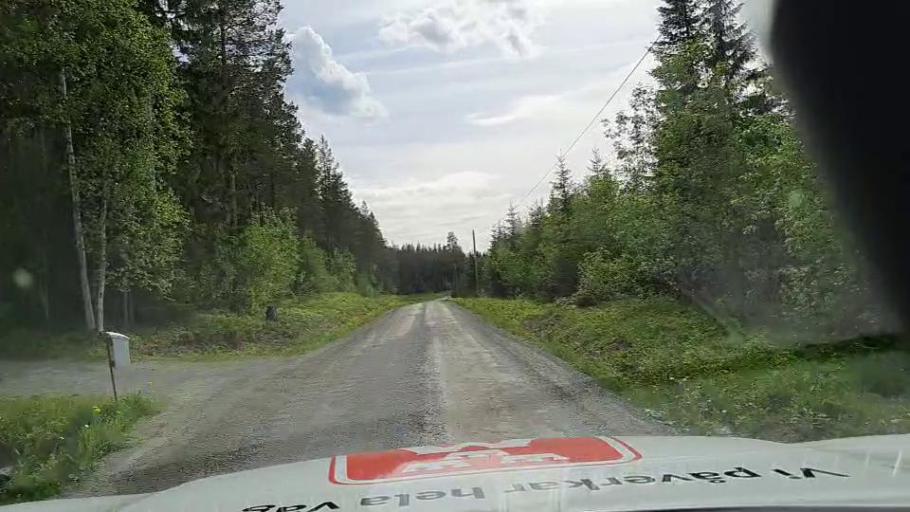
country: SE
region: Jaemtland
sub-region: OEstersunds Kommun
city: Brunflo
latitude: 62.9862
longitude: 14.7124
